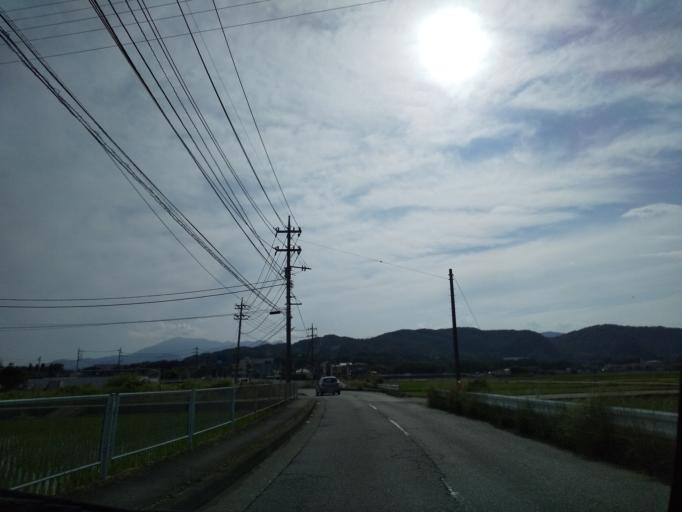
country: JP
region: Kanagawa
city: Zama
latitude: 35.4989
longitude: 139.3482
